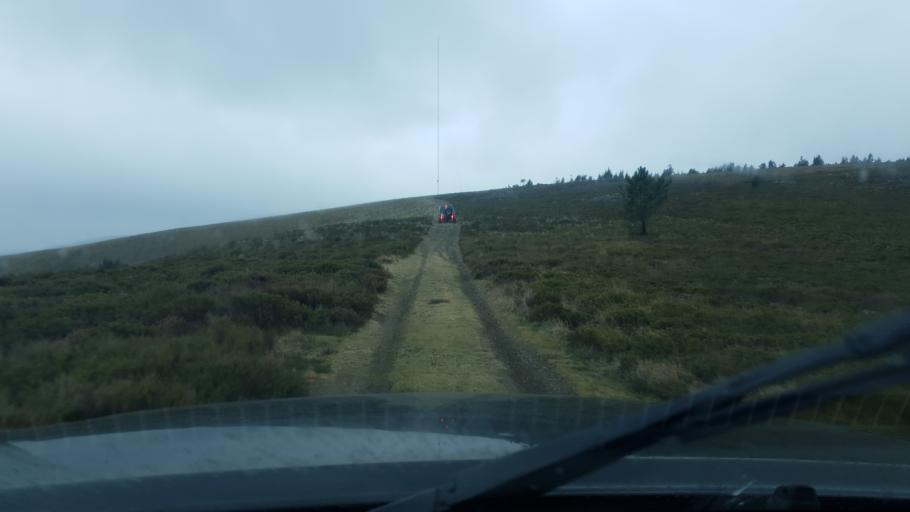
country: PT
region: Viseu
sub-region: Sao Pedro do Sul
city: Sao Pedro do Sul
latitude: 40.8628
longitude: -8.0939
